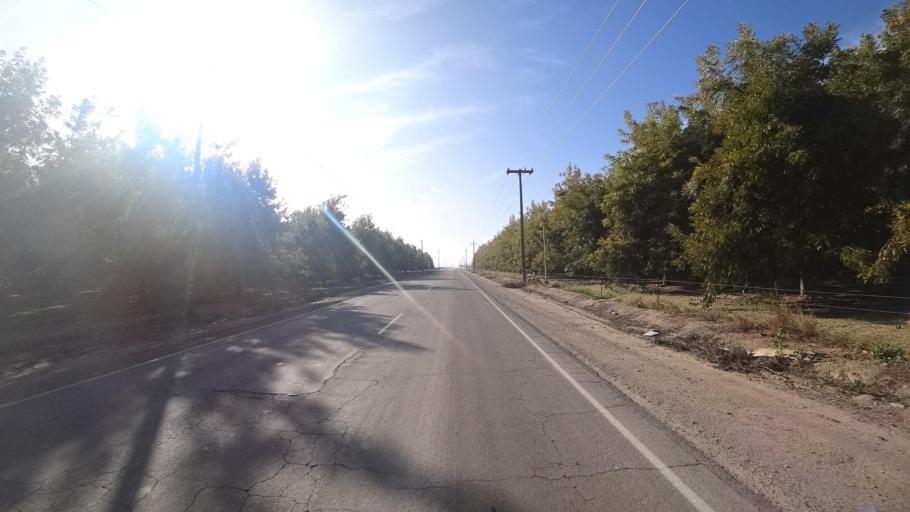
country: US
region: California
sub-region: Kern County
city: McFarland
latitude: 35.6186
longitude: -119.2044
